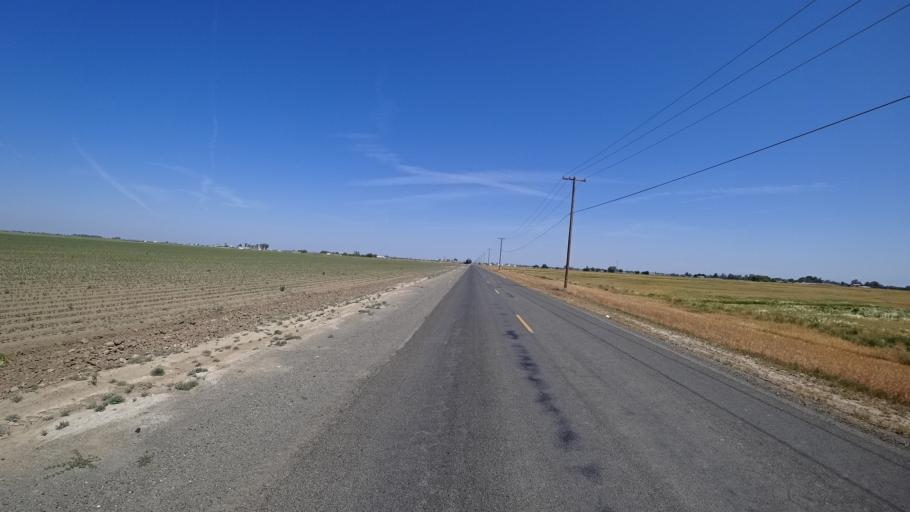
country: US
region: California
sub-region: Kings County
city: Lemoore
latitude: 36.2597
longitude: -119.7990
